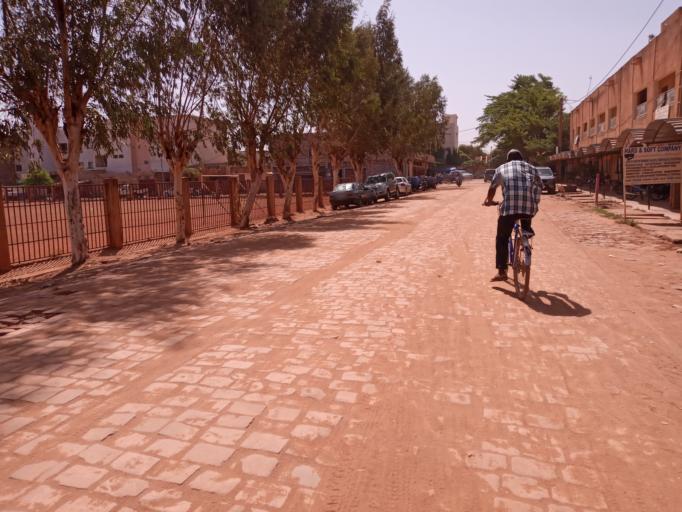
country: ML
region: Bamako
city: Bamako
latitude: 12.5846
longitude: -7.9539
